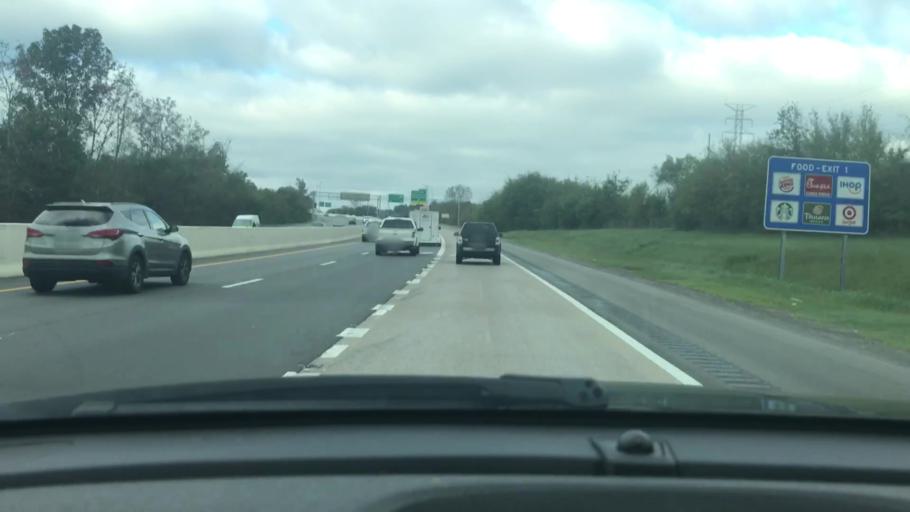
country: US
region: Tennessee
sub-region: Davidson County
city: Goodlettsville
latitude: 36.3120
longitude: -86.6809
